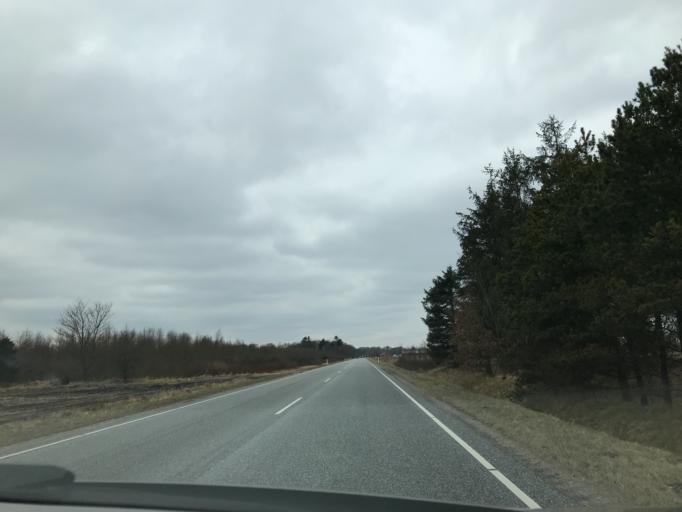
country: DK
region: South Denmark
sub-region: Billund Kommune
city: Grindsted
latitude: 55.8522
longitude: 8.8177
